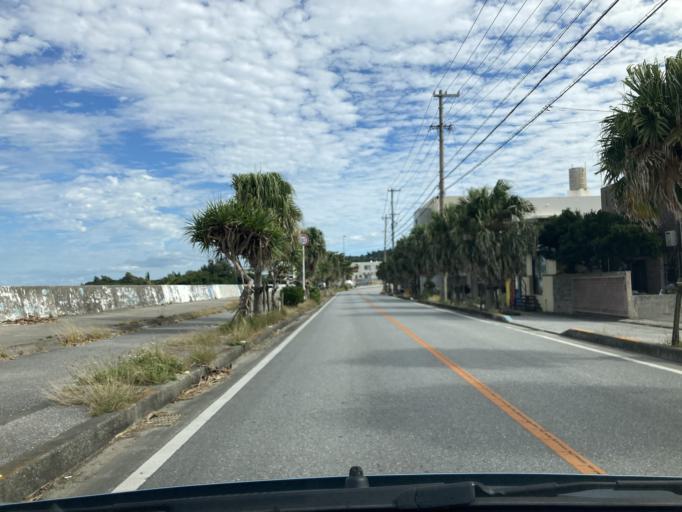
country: JP
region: Okinawa
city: Ishikawa
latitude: 26.4222
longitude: 127.7395
